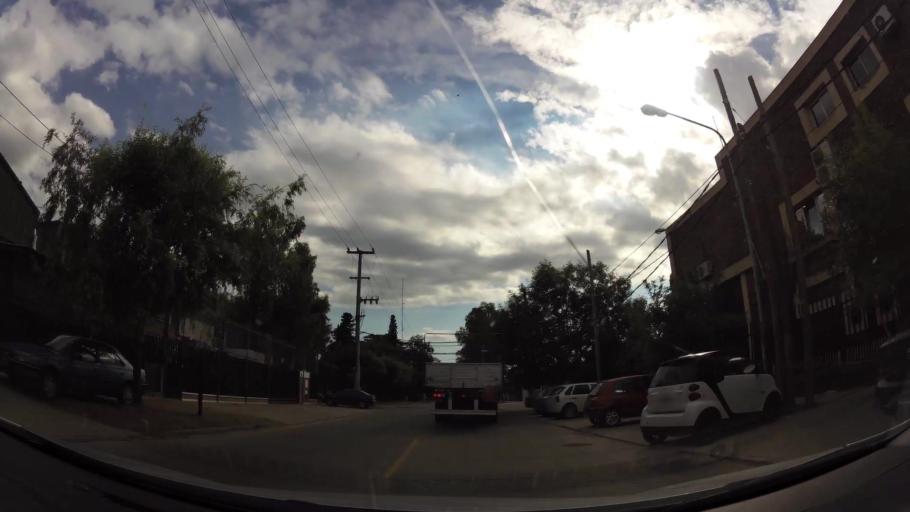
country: AR
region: Buenos Aires
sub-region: Partido de Tigre
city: Tigre
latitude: -34.4802
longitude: -58.6322
